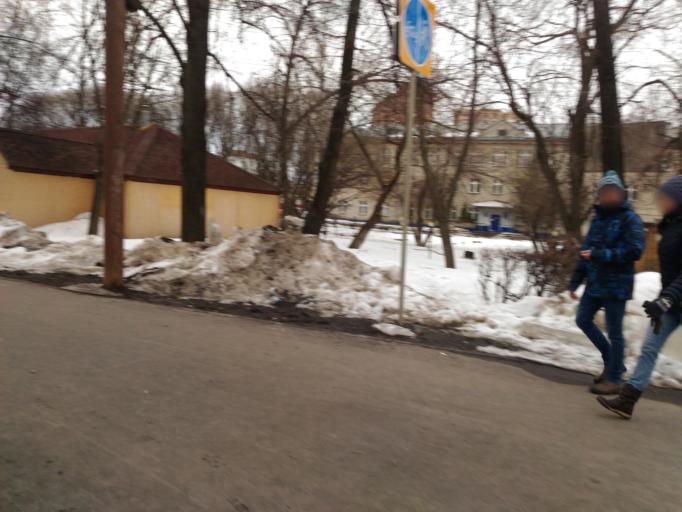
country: RU
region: Ulyanovsk
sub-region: Ulyanovskiy Rayon
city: Ulyanovsk
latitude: 54.3051
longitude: 48.3793
